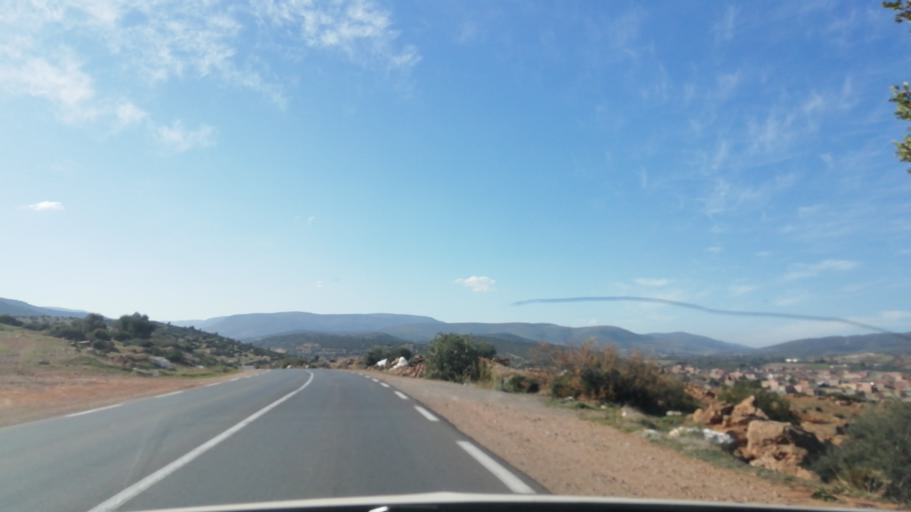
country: DZ
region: Tlemcen
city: Ouled Mimoun
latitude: 34.8715
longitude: -1.1256
